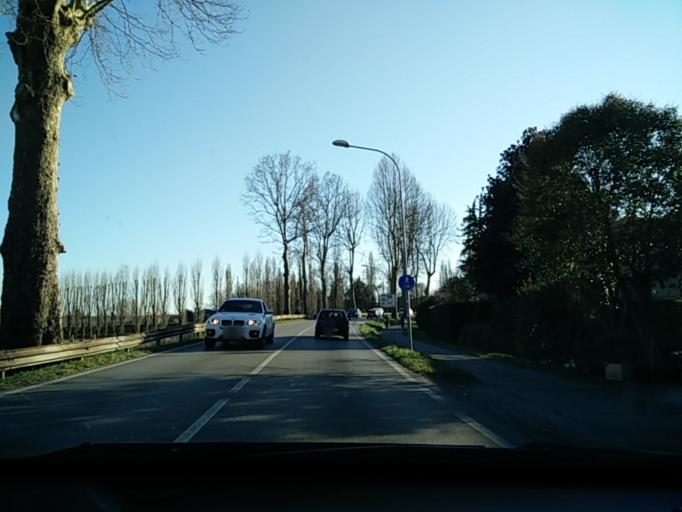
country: IT
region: Veneto
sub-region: Provincia di Treviso
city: Oderzo
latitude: 45.7822
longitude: 12.4990
